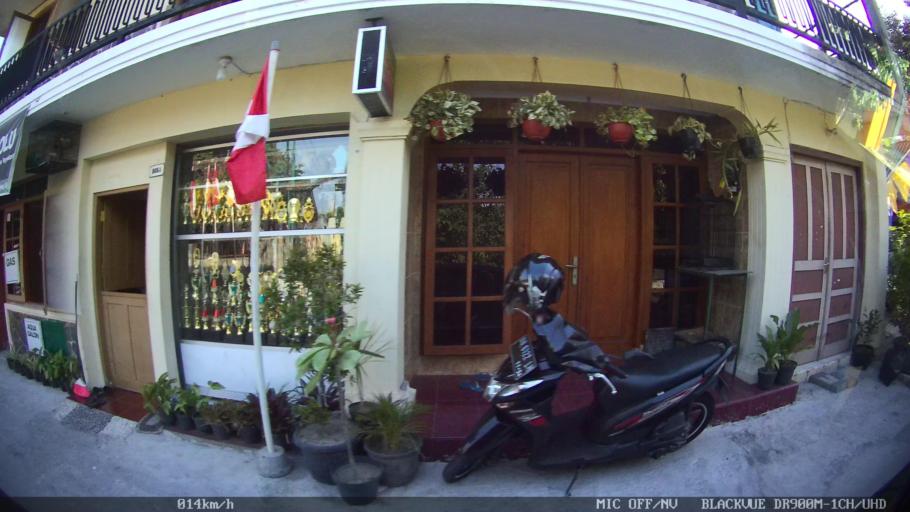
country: ID
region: Daerah Istimewa Yogyakarta
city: Yogyakarta
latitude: -7.8214
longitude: 110.3808
